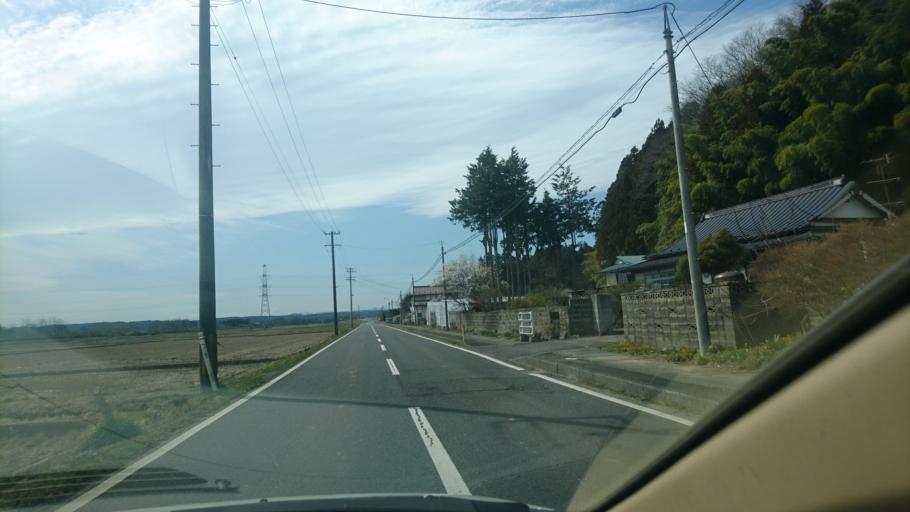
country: JP
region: Miyagi
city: Furukawa
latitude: 38.7459
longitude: 140.9807
